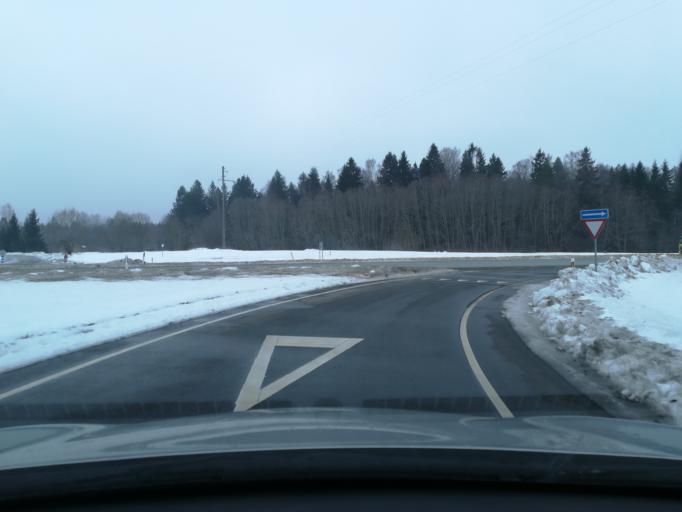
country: EE
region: Harju
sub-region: Loksa linn
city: Loksa
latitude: 59.4641
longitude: 25.7045
